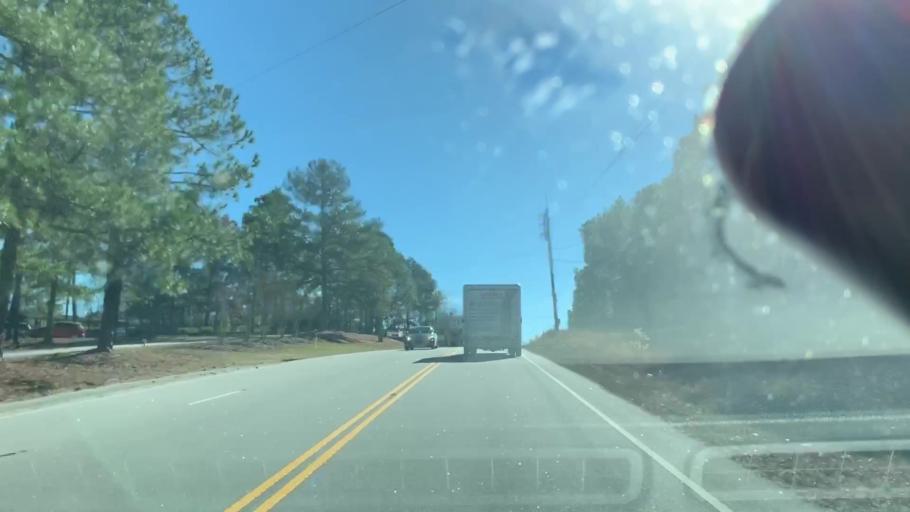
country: US
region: South Carolina
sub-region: Richland County
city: Woodfield
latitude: 34.0902
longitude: -80.8918
